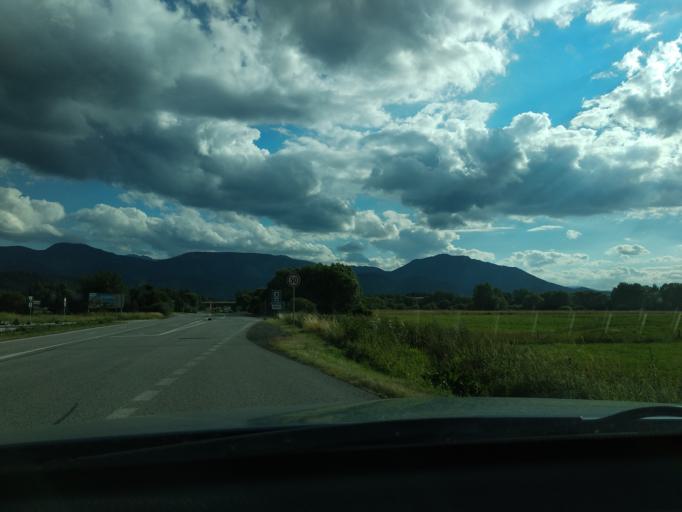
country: SK
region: Zilinsky
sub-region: Okres Zilina
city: Liptovsky Hradok
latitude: 49.0628
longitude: 19.7511
